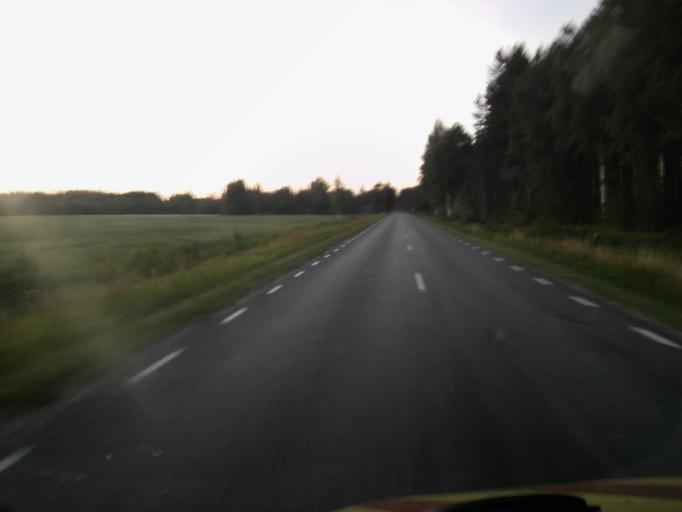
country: EE
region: Paernumaa
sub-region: Paikuse vald
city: Paikuse
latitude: 58.3041
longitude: 24.6876
